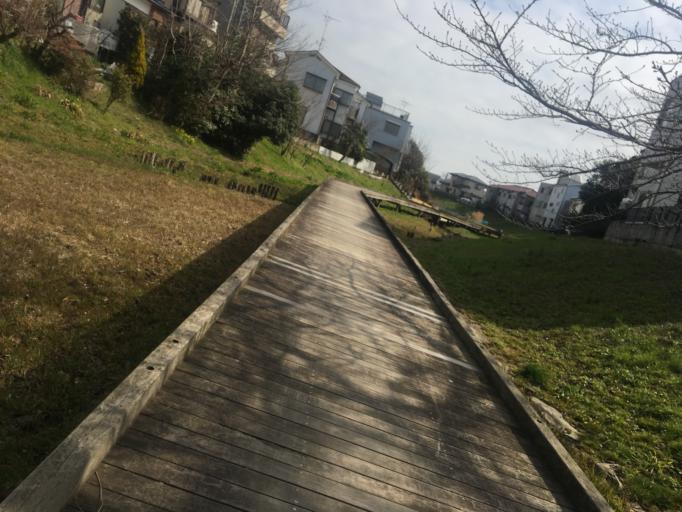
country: JP
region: Saitama
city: Shiki
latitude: 35.8426
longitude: 139.5724
